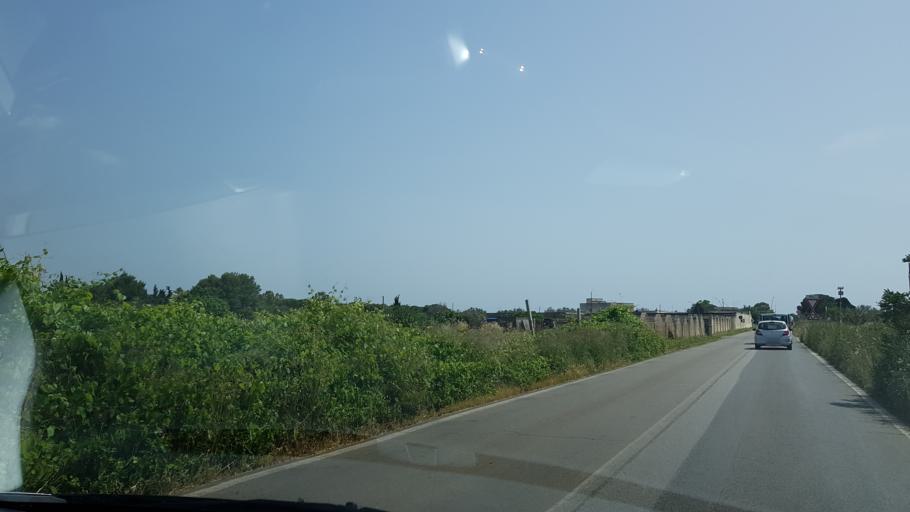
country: IT
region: Apulia
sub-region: Provincia di Lecce
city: Porto Cesareo
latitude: 40.3047
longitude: 17.8610
